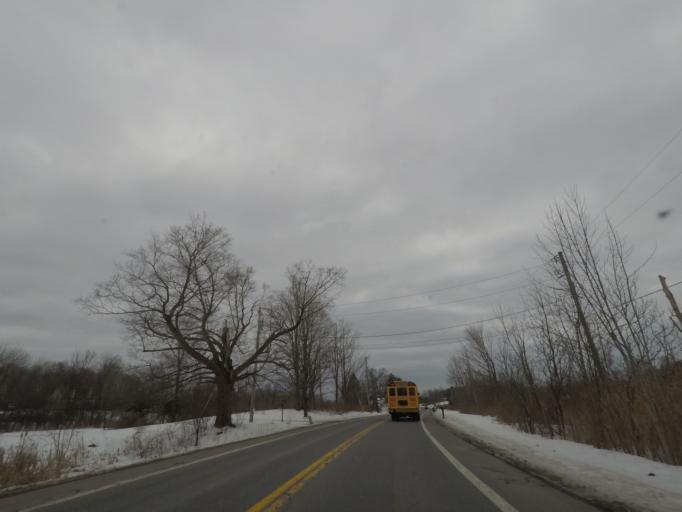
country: US
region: New York
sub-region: Saratoga County
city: Stillwater
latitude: 42.9641
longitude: -73.6746
